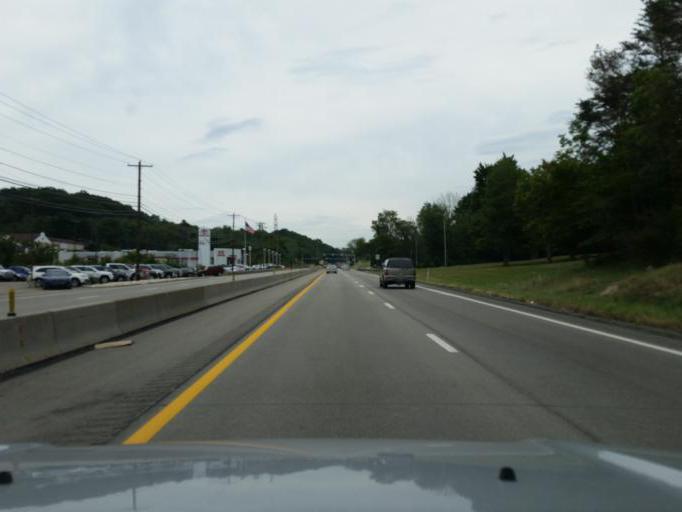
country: US
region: Pennsylvania
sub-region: Westmoreland County
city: Greensburg
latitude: 40.2988
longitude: -79.4843
